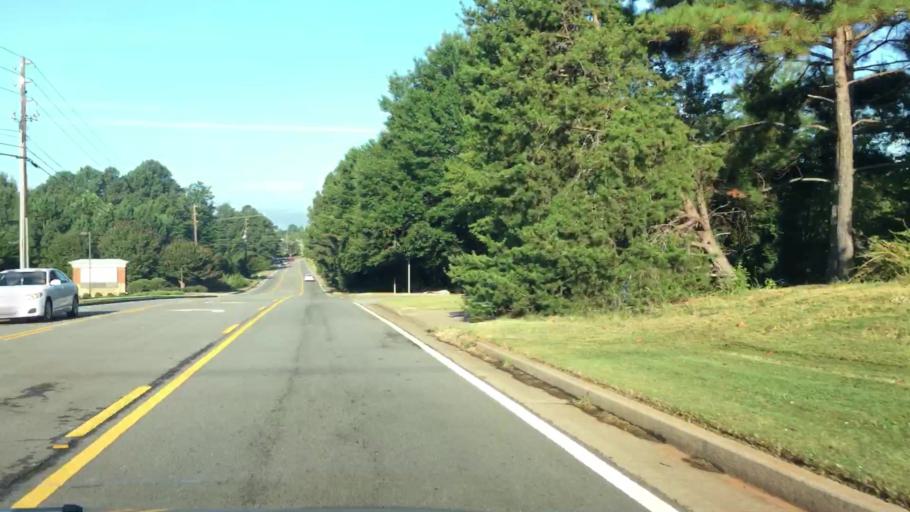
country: US
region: Georgia
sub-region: Clayton County
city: Morrow
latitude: 33.5603
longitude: -84.3167
